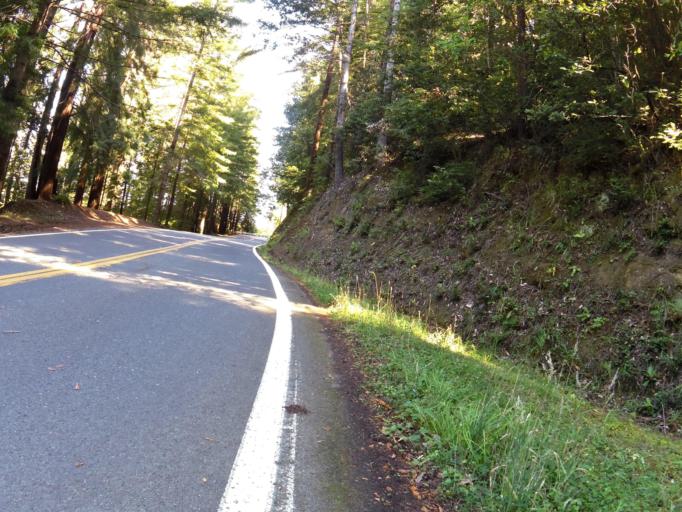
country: US
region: California
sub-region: Mendocino County
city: Fort Bragg
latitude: 39.7270
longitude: -123.8126
